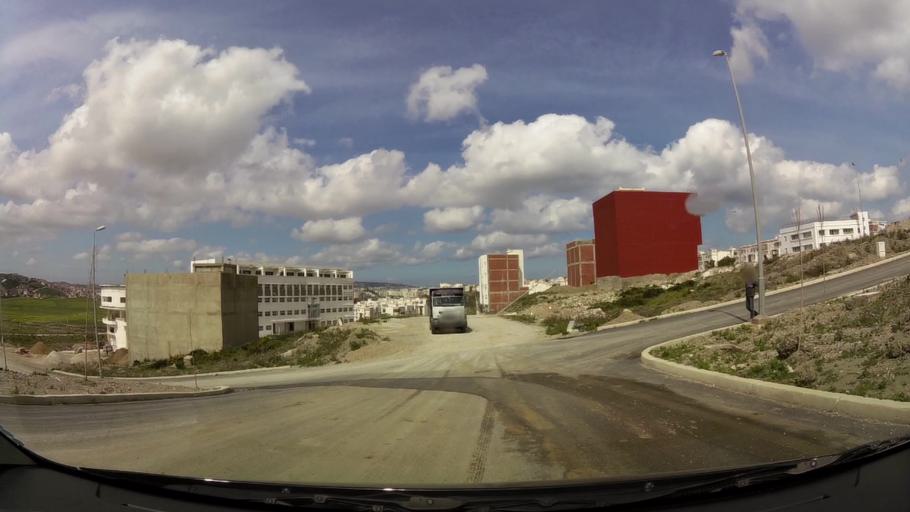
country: MA
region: Tanger-Tetouan
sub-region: Tanger-Assilah
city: Tangier
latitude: 35.7586
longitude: -5.7609
